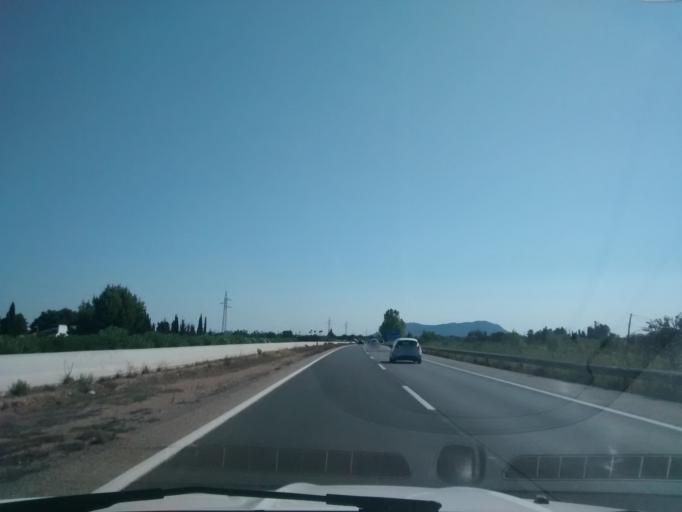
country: ES
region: Balearic Islands
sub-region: Illes Balears
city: Lloseta
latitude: 39.6975
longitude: 2.8827
